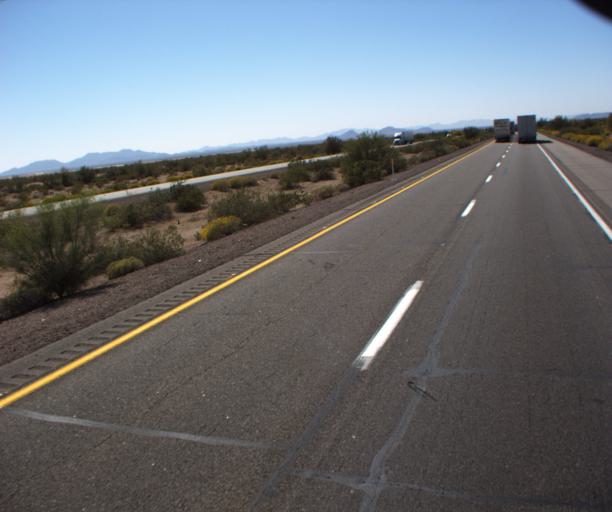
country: US
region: Arizona
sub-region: Yuma County
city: Wellton
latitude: 32.7215
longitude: -113.7703
